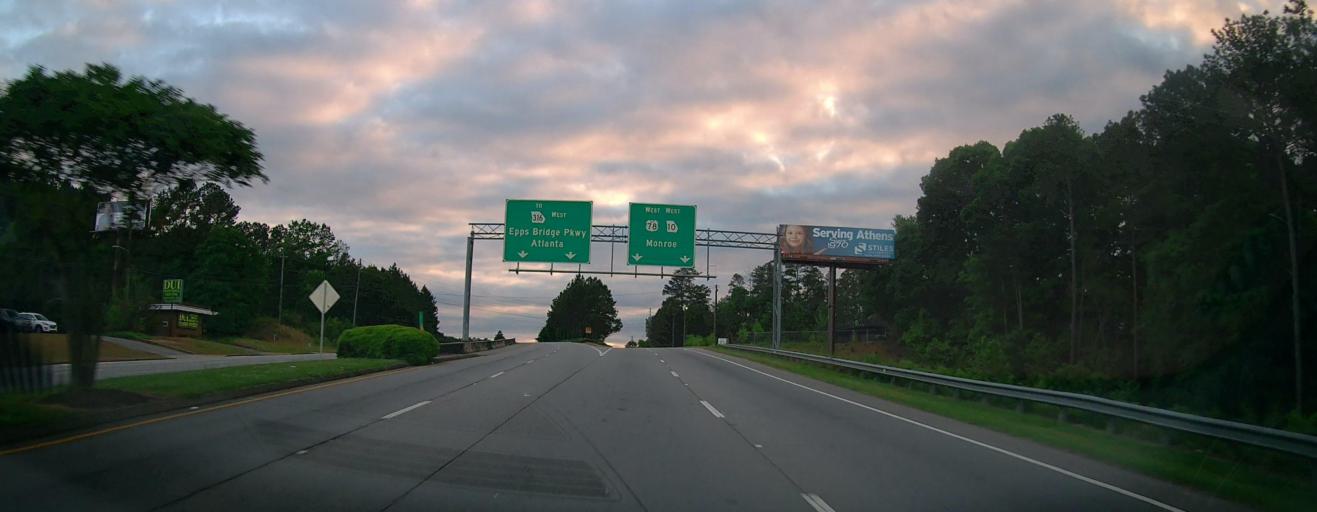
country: US
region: Georgia
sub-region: Clarke County
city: Country Club Estates
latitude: 33.9463
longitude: -83.4293
